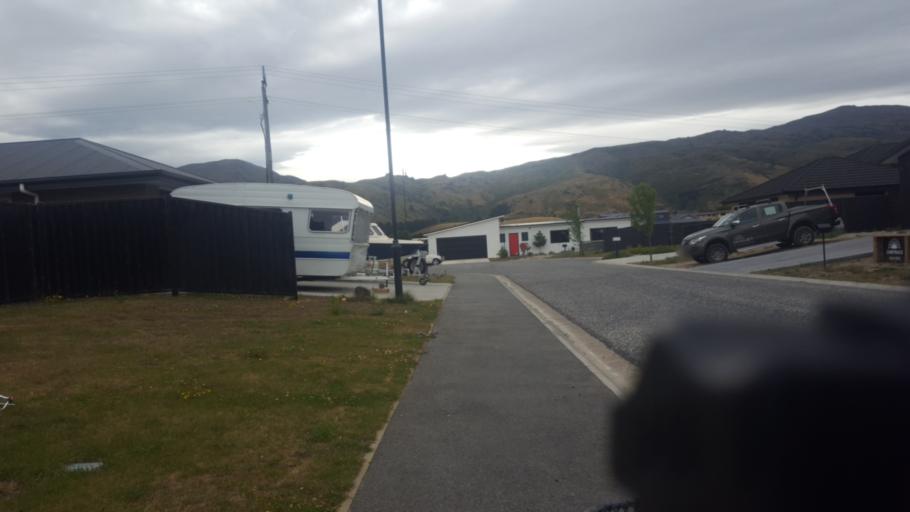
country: NZ
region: Otago
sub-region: Queenstown-Lakes District
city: Wanaka
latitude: -45.0476
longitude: 169.1782
